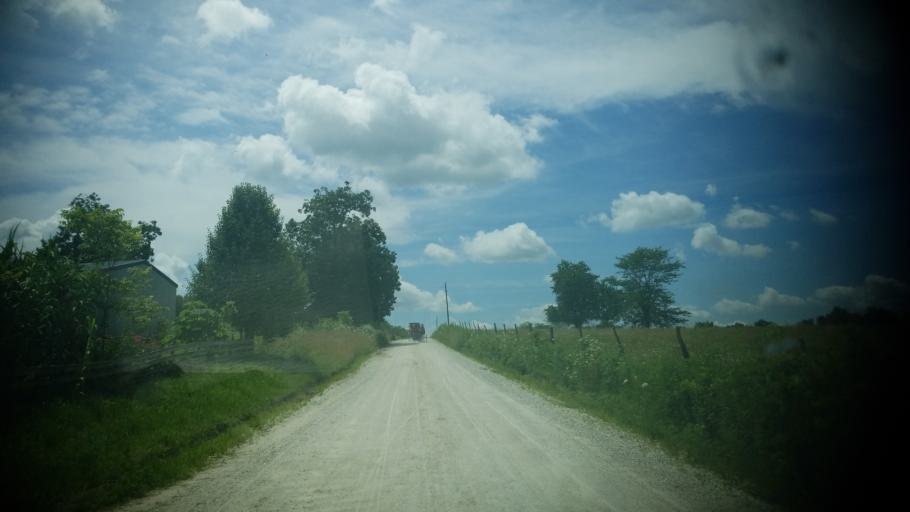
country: US
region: Missouri
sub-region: Pike County
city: Bowling Green
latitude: 39.3081
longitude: -91.2948
